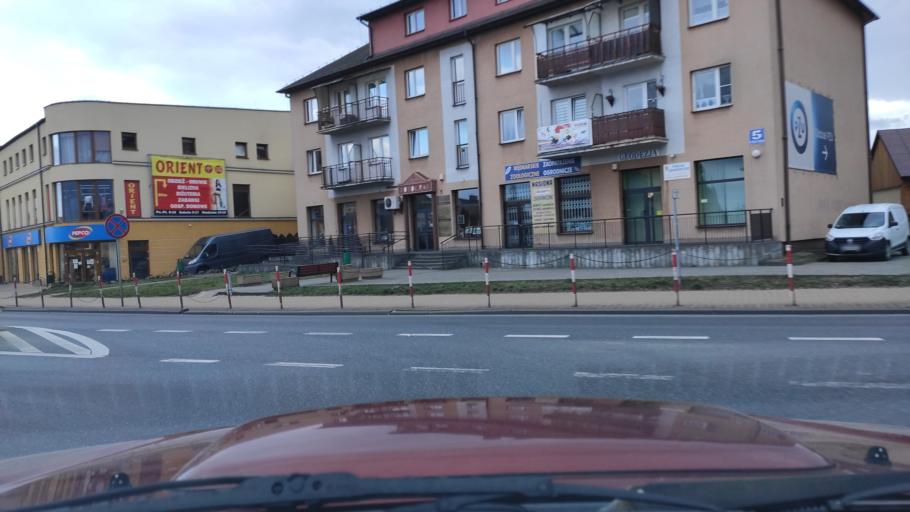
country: PL
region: Masovian Voivodeship
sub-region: Powiat zwolenski
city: Zwolen
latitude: 51.3575
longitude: 21.5824
